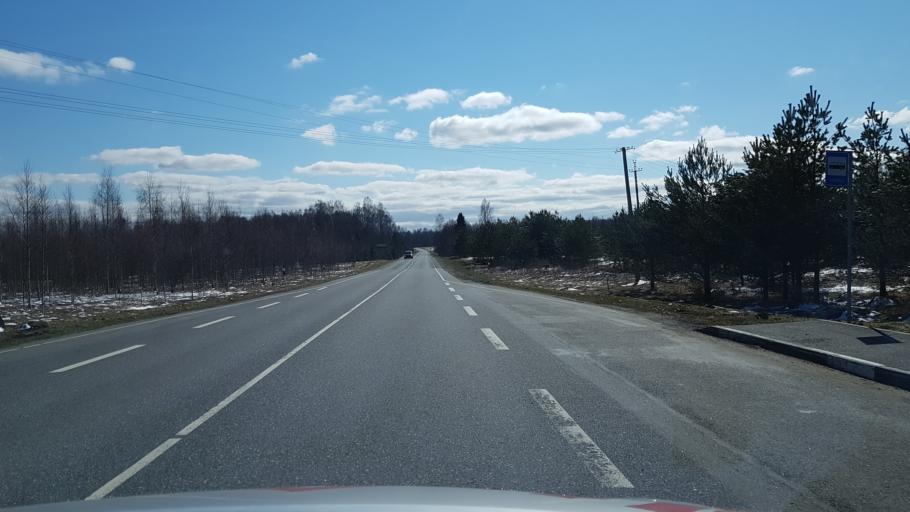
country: EE
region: Laeaene-Virumaa
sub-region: Tapa vald
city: Tapa
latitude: 59.4517
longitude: 25.9453
